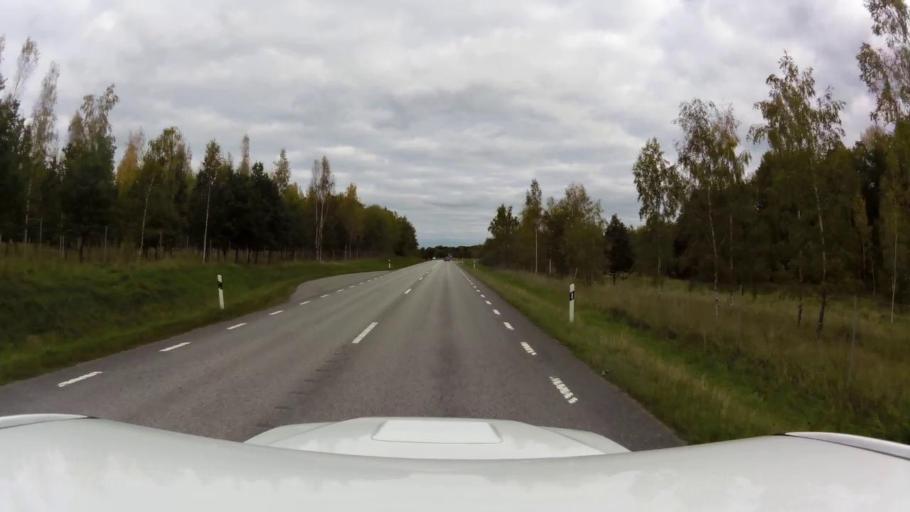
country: SE
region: OEstergoetland
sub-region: Kinda Kommun
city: Rimforsa
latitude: 58.2047
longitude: 15.6686
